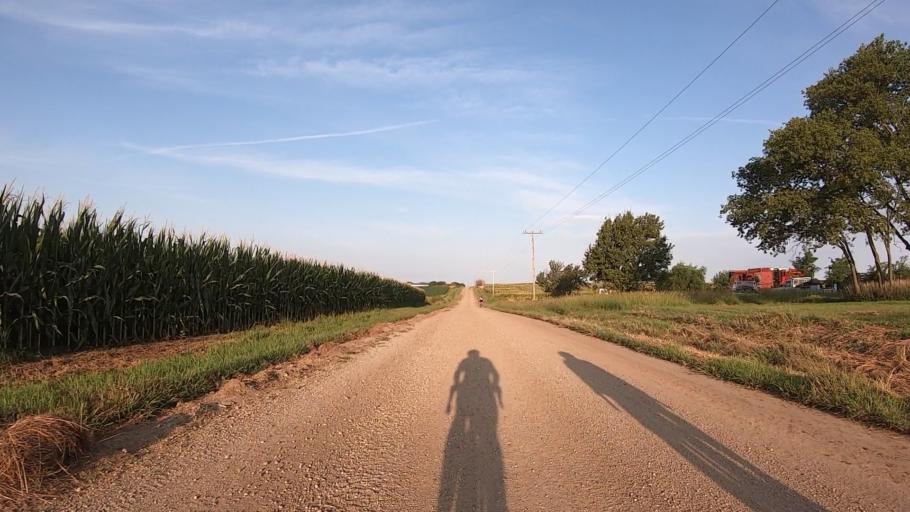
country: US
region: Kansas
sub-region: Marshall County
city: Marysville
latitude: 39.7695
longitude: -96.7391
